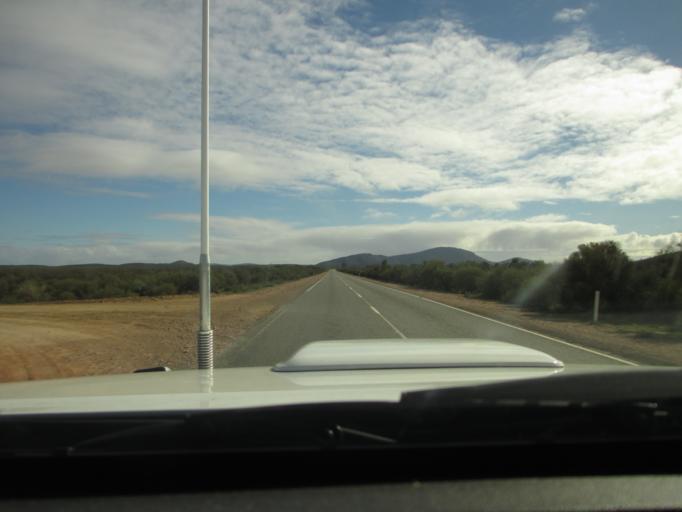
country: AU
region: South Australia
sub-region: Flinders Ranges
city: Quorn
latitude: -31.8415
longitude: 138.3914
